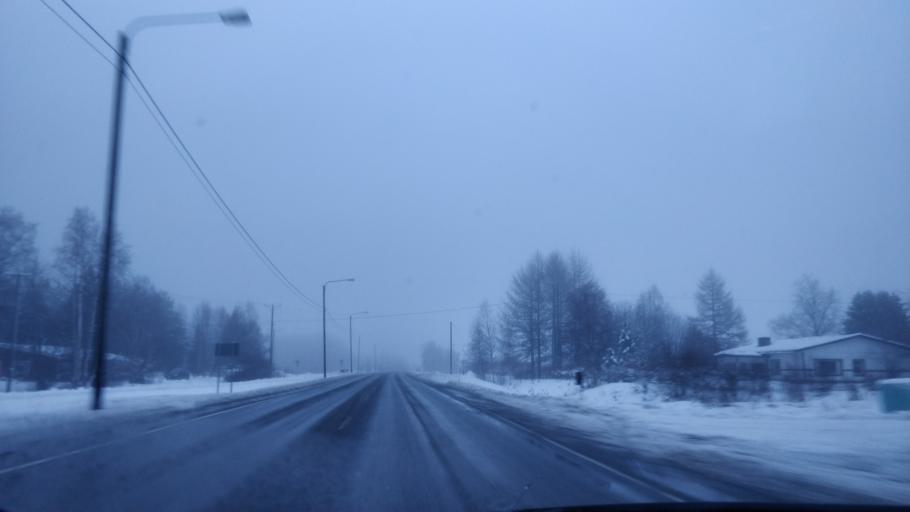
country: FI
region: Lapland
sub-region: Kemi-Tornio
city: Tervola
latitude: 66.1470
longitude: 24.9680
